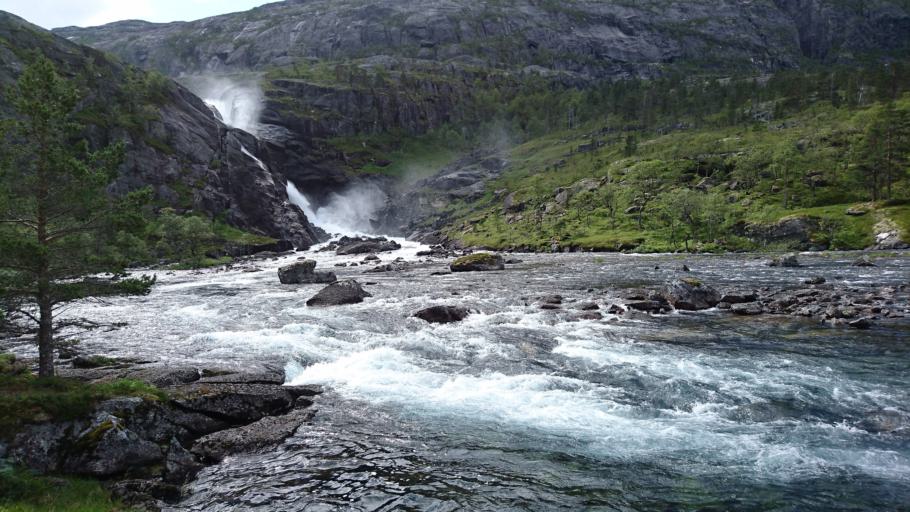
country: NO
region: Hordaland
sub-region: Ullensvang
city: Kinsarvik
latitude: 60.3453
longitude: 6.7900
